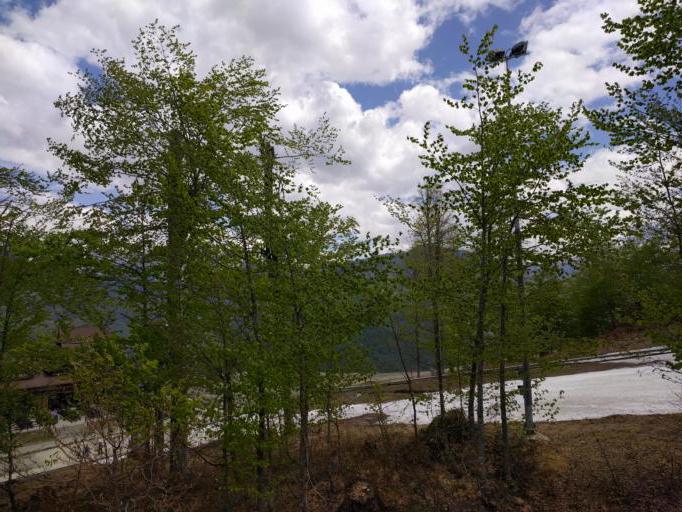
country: RU
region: Krasnodarskiy
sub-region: Sochi City
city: Krasnaya Polyana
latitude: 43.6574
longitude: 40.3191
